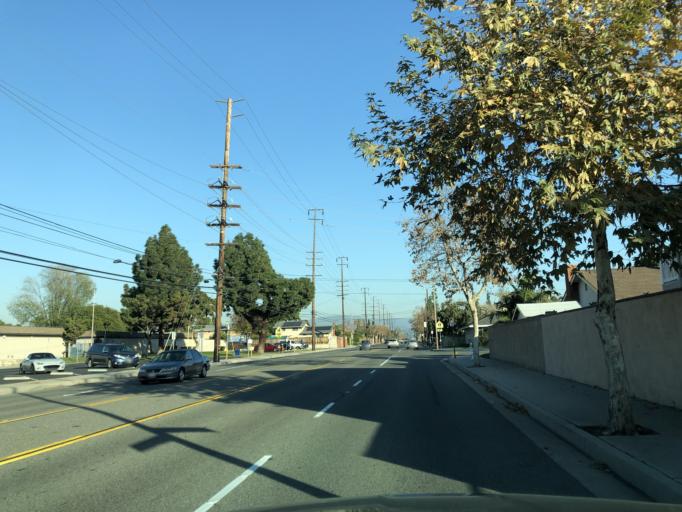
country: US
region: California
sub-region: Orange County
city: Orange
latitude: 33.7732
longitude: -117.8505
